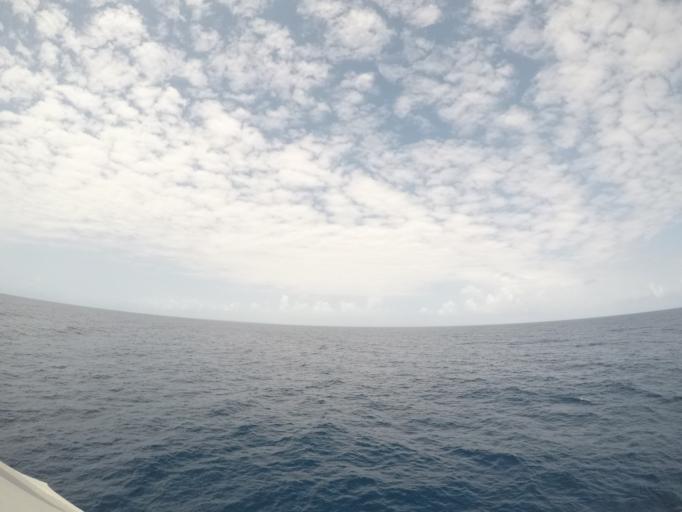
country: TZ
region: Zanzibar North
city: Nungwi
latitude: -5.5849
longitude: 39.3552
